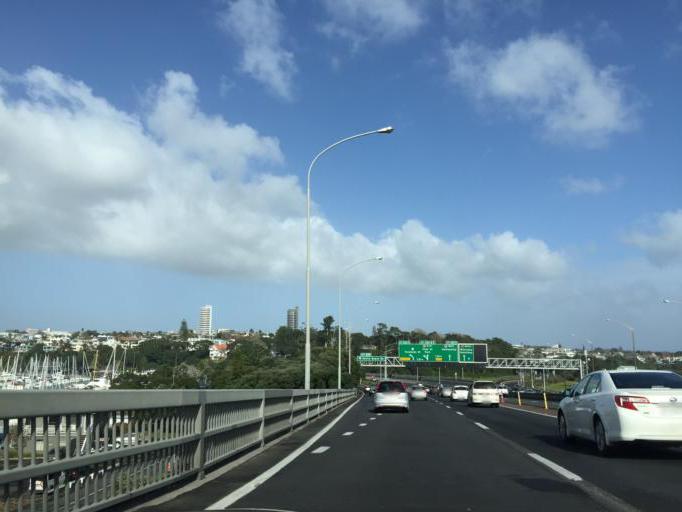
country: NZ
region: Auckland
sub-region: Auckland
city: North Shore
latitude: -36.8349
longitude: 174.7430
